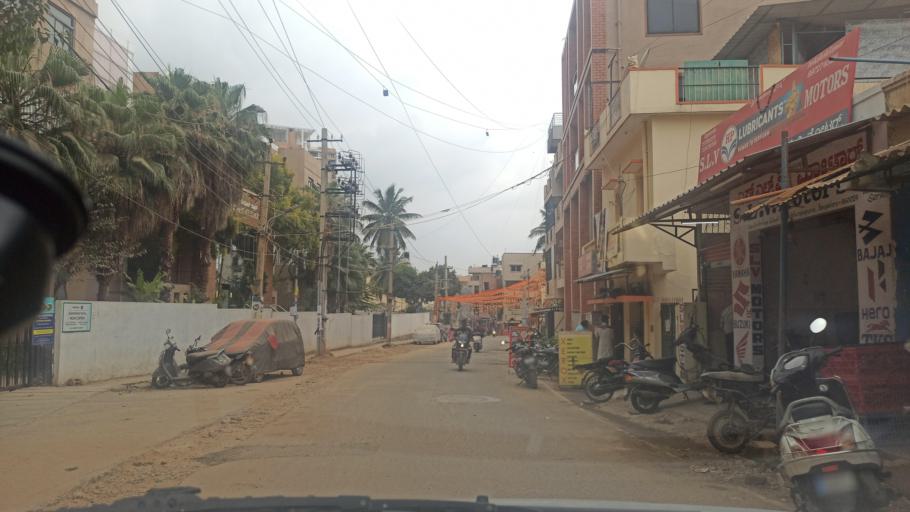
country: IN
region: Karnataka
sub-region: Bangalore Urban
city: Yelahanka
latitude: 13.0490
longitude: 77.6010
